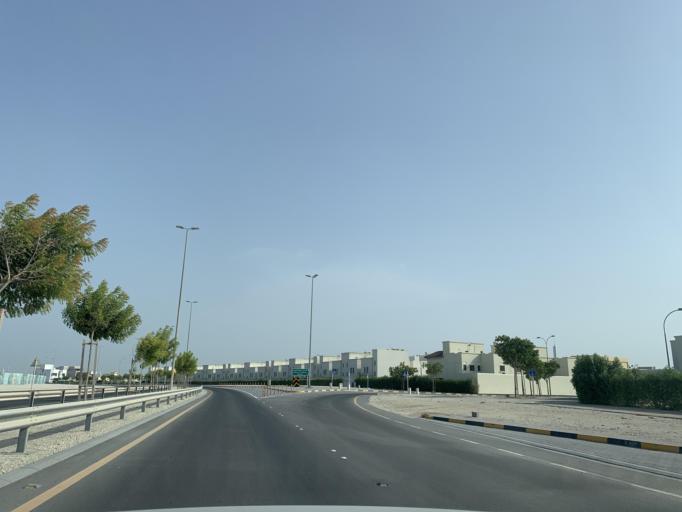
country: BH
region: Muharraq
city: Al Muharraq
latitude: 26.3164
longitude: 50.6316
